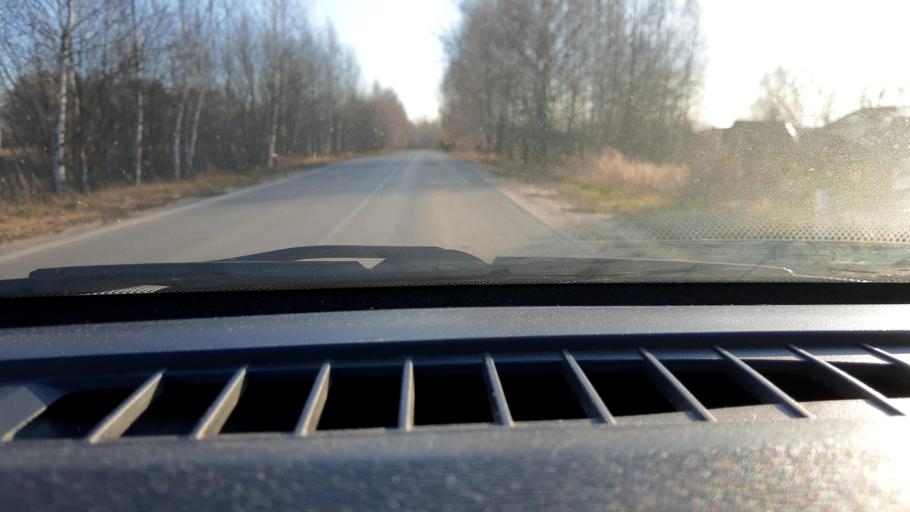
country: RU
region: Nizjnij Novgorod
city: Neklyudovo
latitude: 56.4759
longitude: 43.8762
